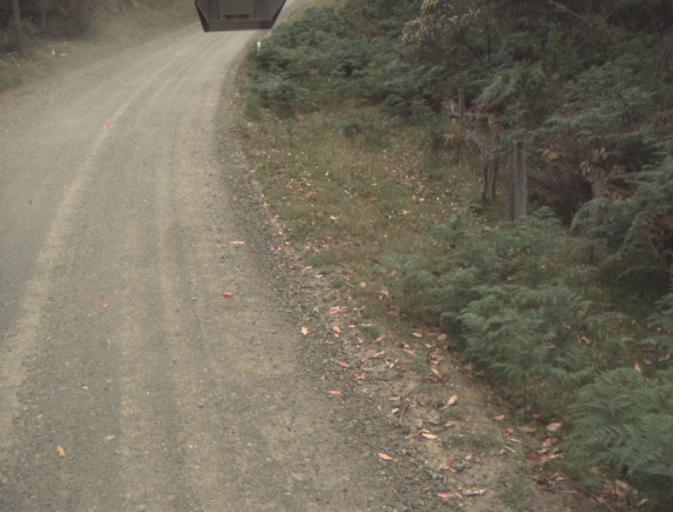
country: AU
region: Tasmania
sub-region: Dorset
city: Scottsdale
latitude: -41.4088
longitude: 147.5176
